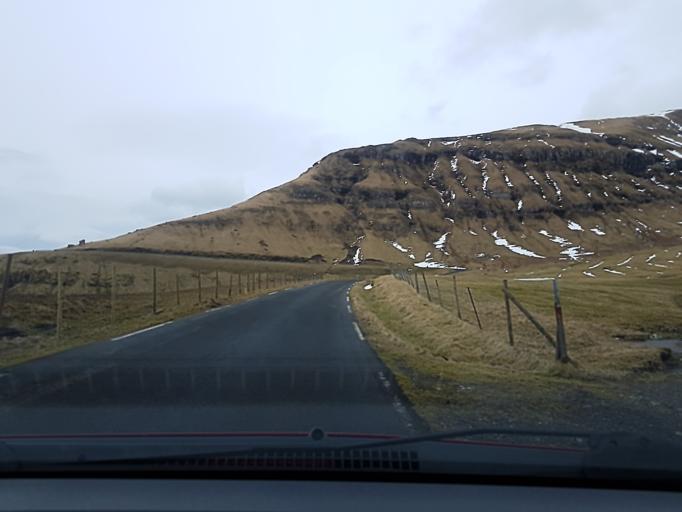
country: FO
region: Streymoy
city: Hoyvik
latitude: 61.9973
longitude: -6.8893
